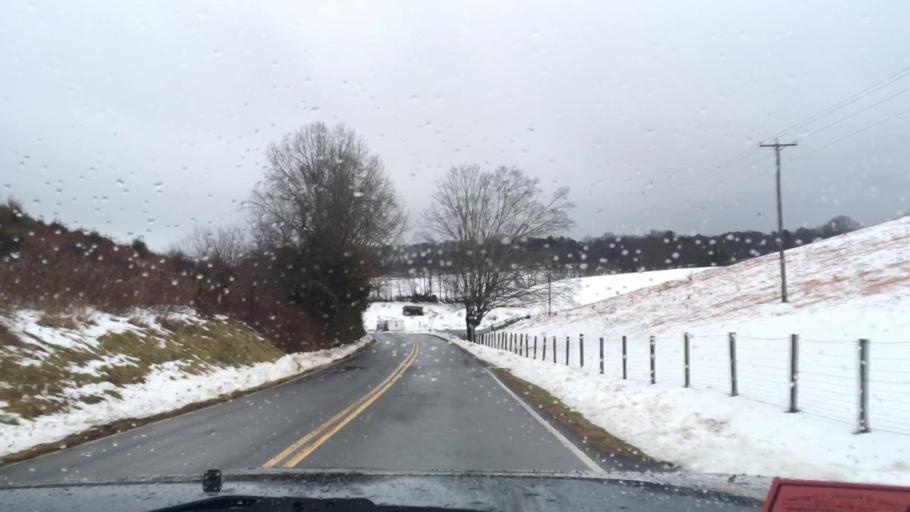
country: US
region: Virginia
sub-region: Pulaski County
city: Dublin
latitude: 37.0103
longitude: -80.6560
